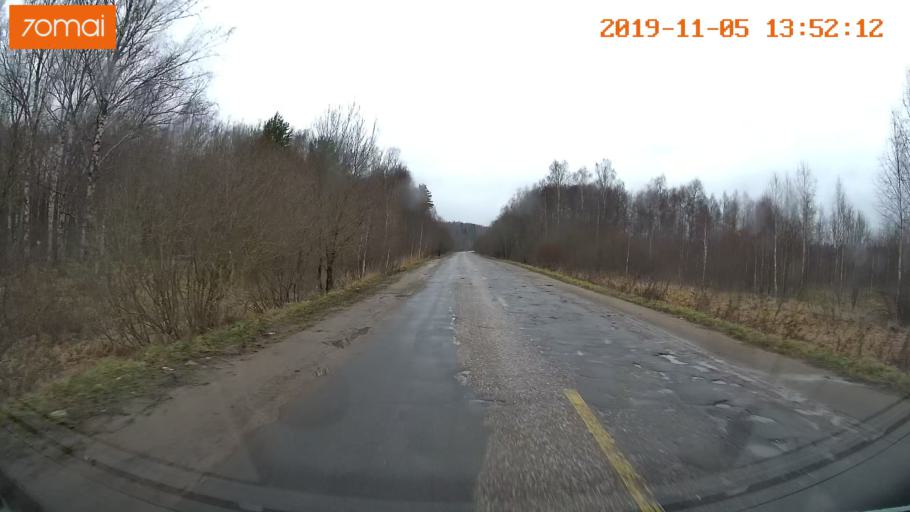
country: RU
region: Ivanovo
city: Kaminskiy
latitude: 57.0269
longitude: 41.3897
